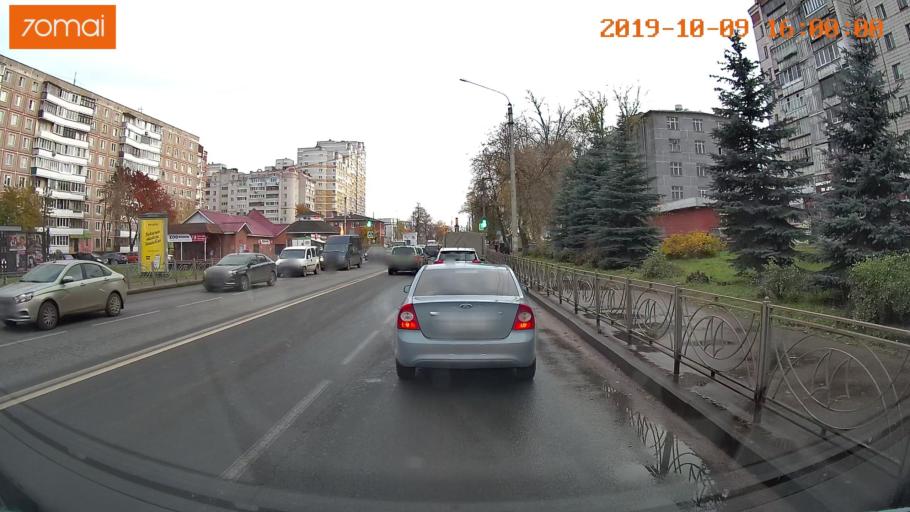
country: RU
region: Kostroma
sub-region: Kostromskoy Rayon
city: Kostroma
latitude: 57.7664
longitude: 40.9510
